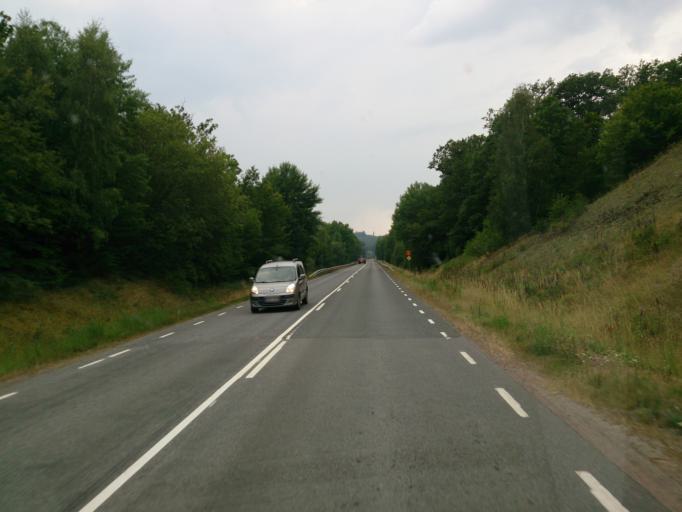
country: SE
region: Skane
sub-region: Kristianstads Kommun
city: Tollarp
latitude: 56.1763
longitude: 14.2887
